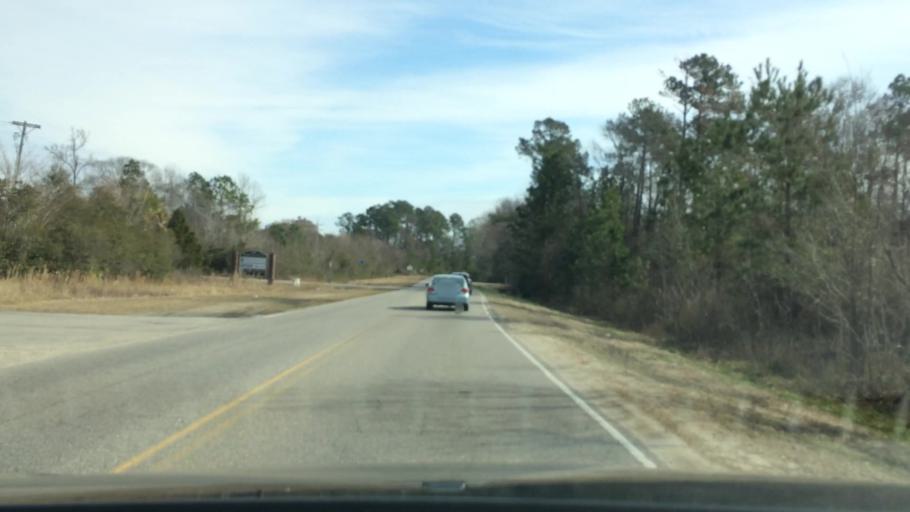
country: US
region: South Carolina
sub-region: Horry County
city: Socastee
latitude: 33.6780
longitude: -78.9722
